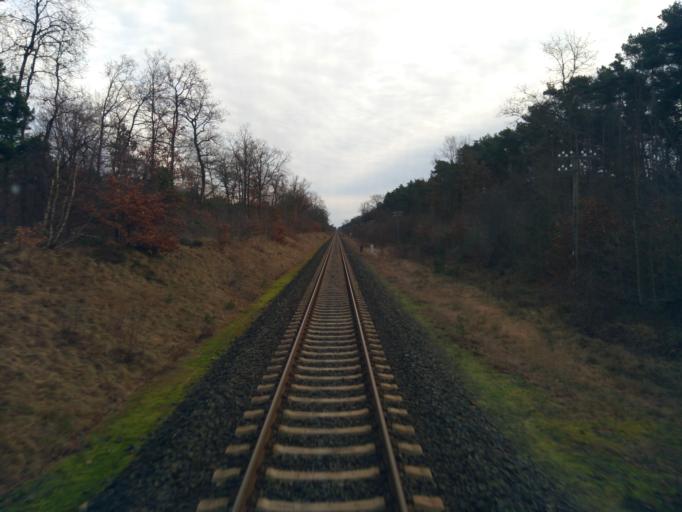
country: DE
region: Lower Saxony
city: Munster
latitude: 52.9938
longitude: 10.1675
